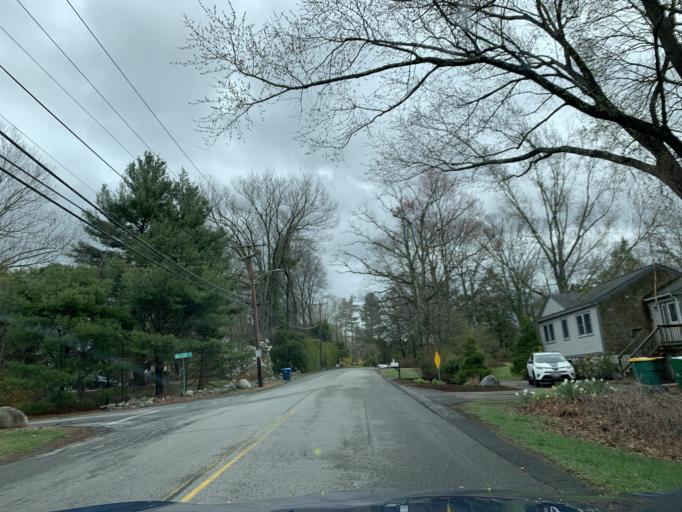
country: US
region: Massachusetts
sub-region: Bristol County
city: Attleboro
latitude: 41.9636
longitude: -71.2384
